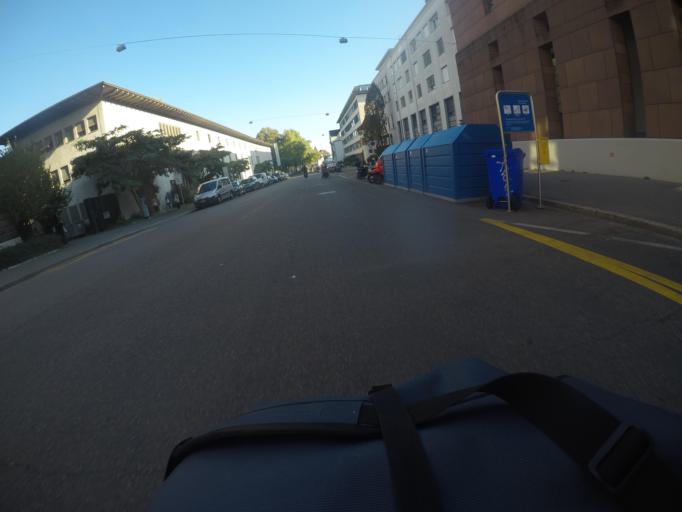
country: CH
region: Basel-City
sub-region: Basel-Stadt
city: Basel
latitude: 47.5576
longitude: 7.5845
